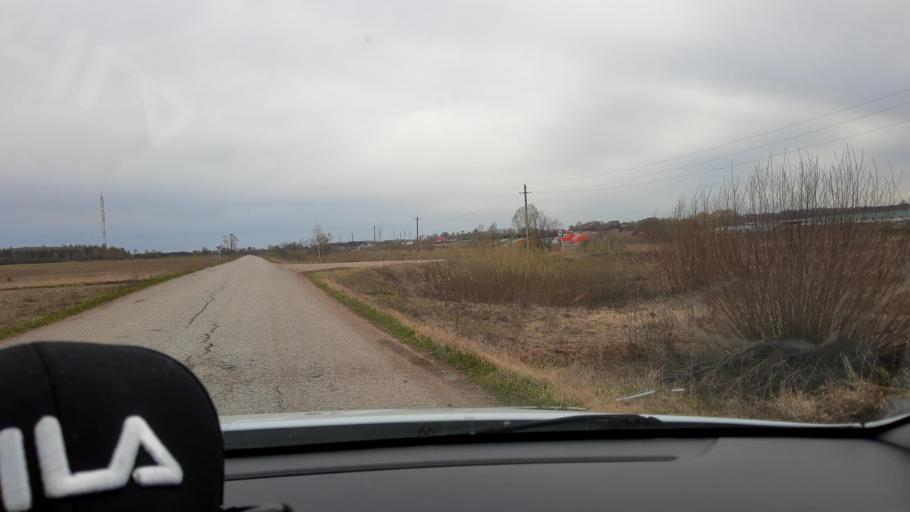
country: RU
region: Bashkortostan
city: Iglino
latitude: 54.7790
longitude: 56.5039
